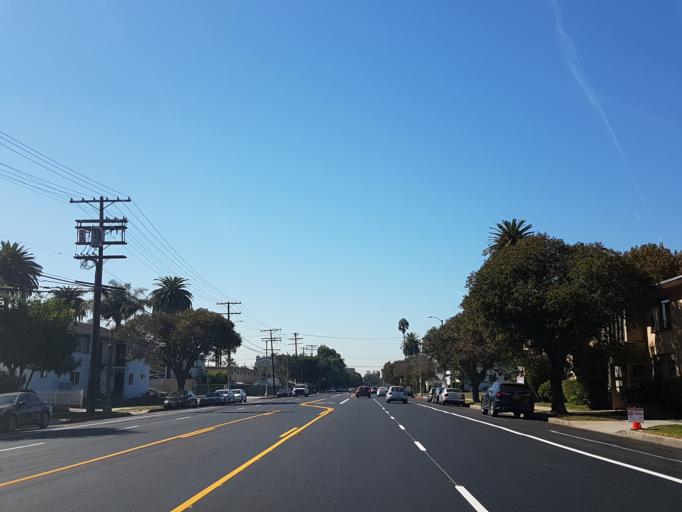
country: US
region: California
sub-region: Los Angeles County
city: Culver City
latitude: 34.0031
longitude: -118.4235
